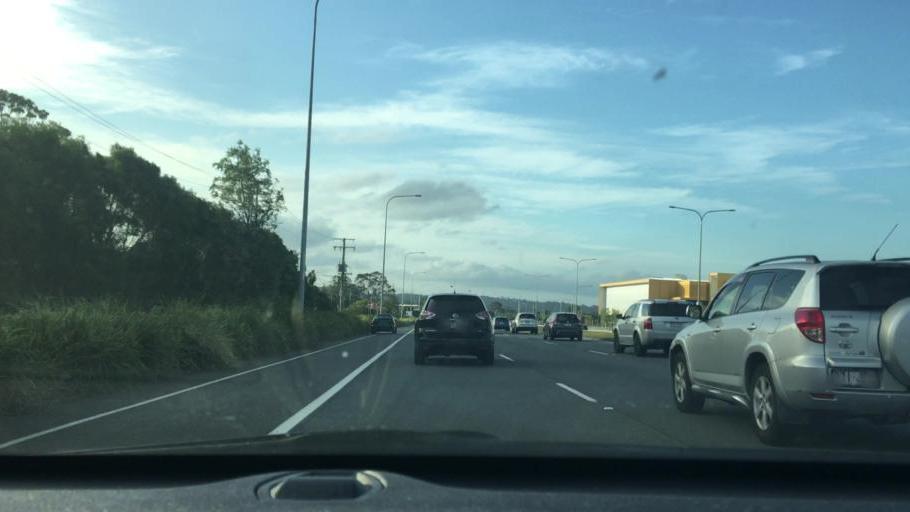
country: AU
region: Queensland
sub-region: Gold Coast
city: Nerang
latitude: -28.0078
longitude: 153.3654
